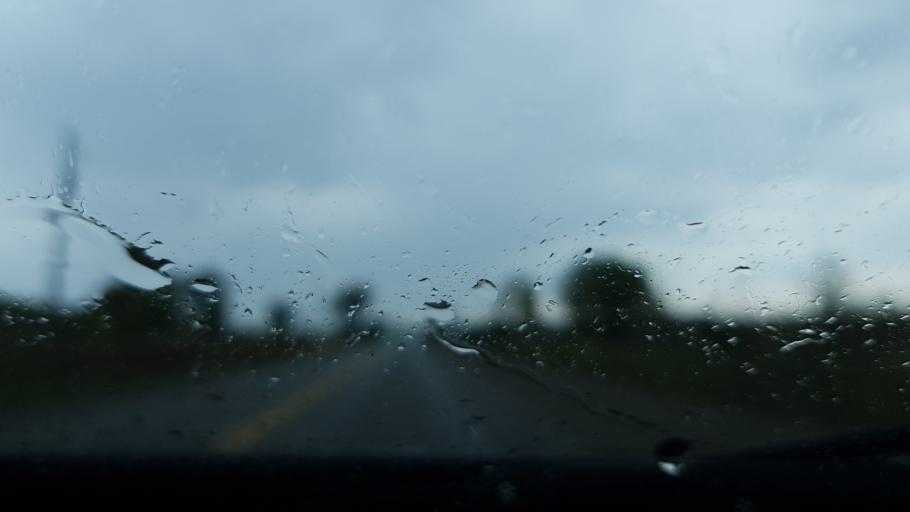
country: CA
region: Ontario
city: Omemee
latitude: 44.3849
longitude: -78.5973
